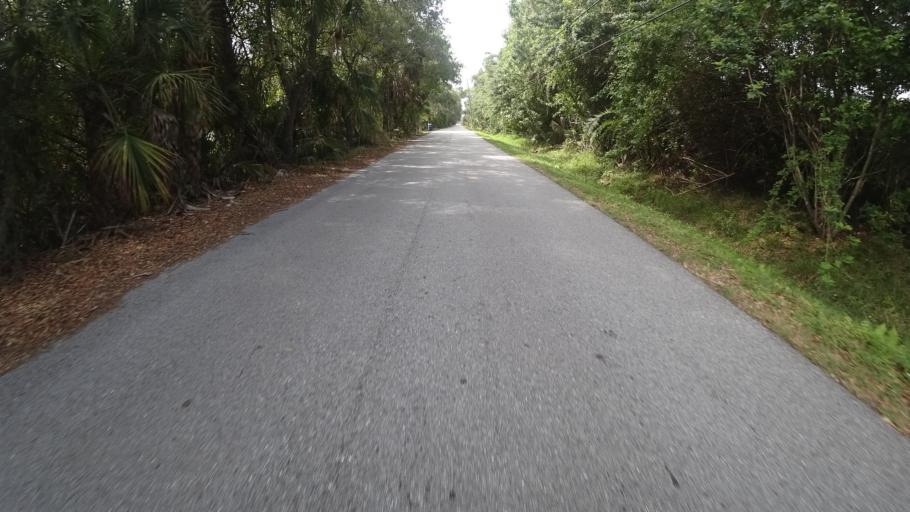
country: US
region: Florida
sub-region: Sarasota County
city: North Sarasota
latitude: 27.4014
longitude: -82.5301
